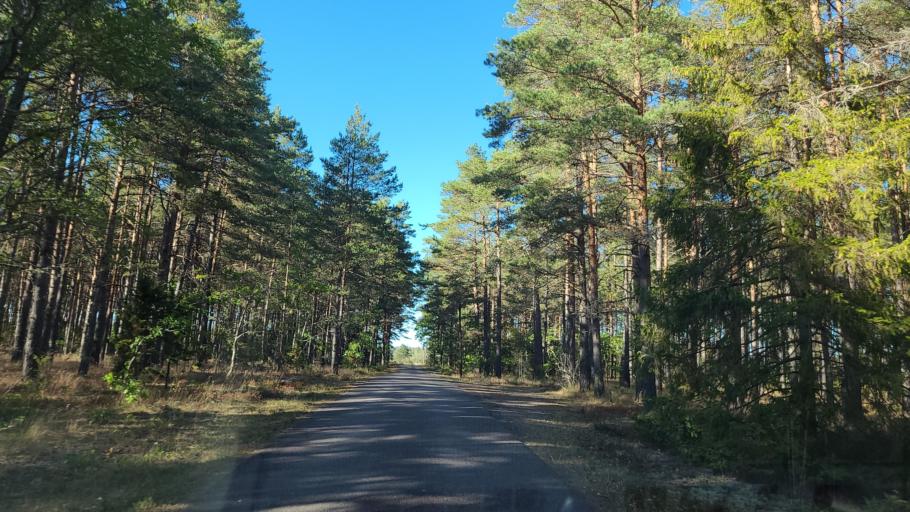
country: SE
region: Kalmar
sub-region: Borgholms Kommun
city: Borgholm
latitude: 57.3152
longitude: 17.0506
